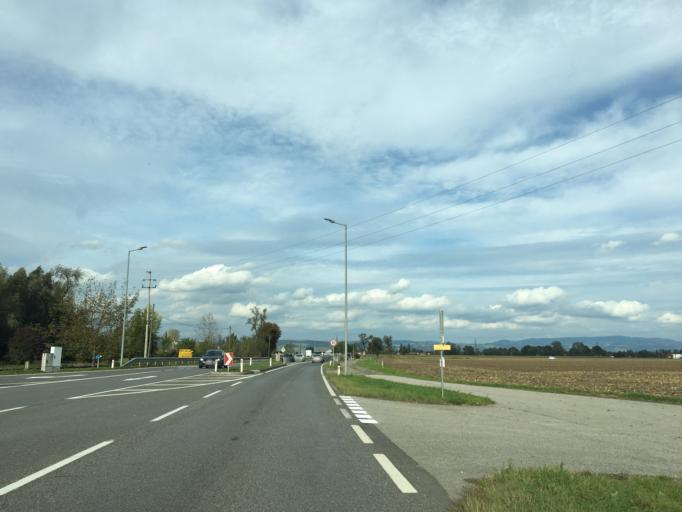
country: AT
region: Upper Austria
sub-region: Wels-Land
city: Buchkirchen
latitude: 48.2869
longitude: 14.0072
